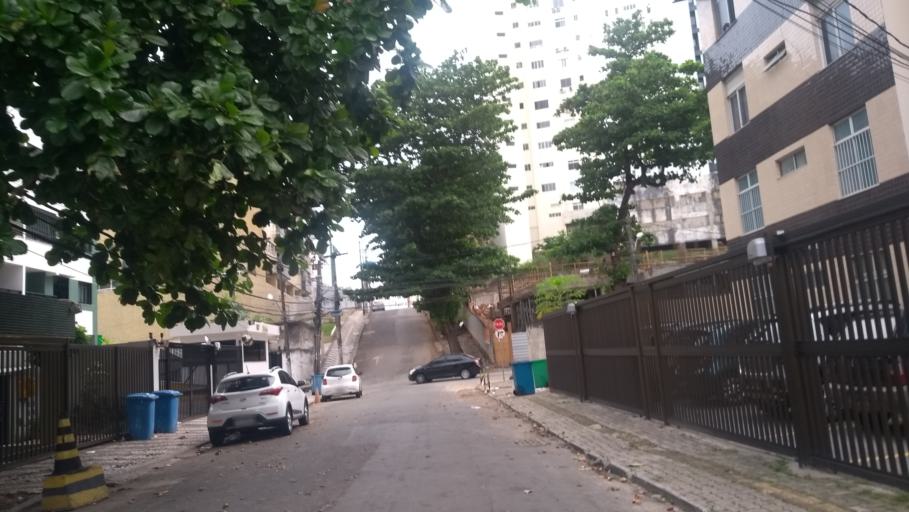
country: BR
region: Bahia
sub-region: Salvador
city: Salvador
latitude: -12.9920
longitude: -38.4466
